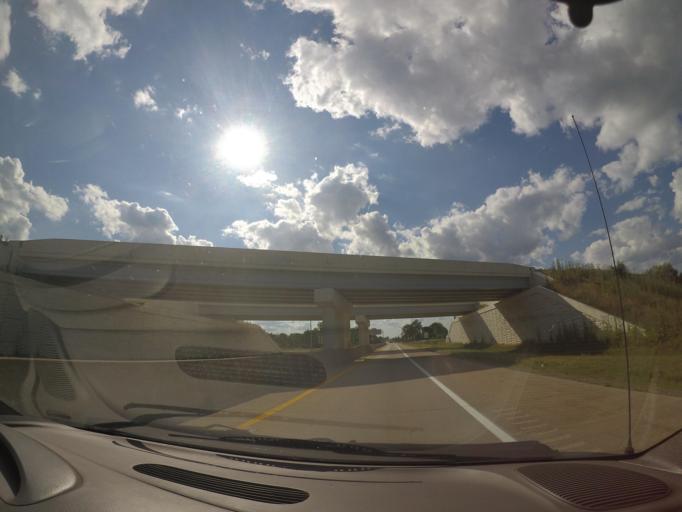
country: US
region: Ohio
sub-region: Wood County
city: Luckey
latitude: 41.4915
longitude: -83.4633
